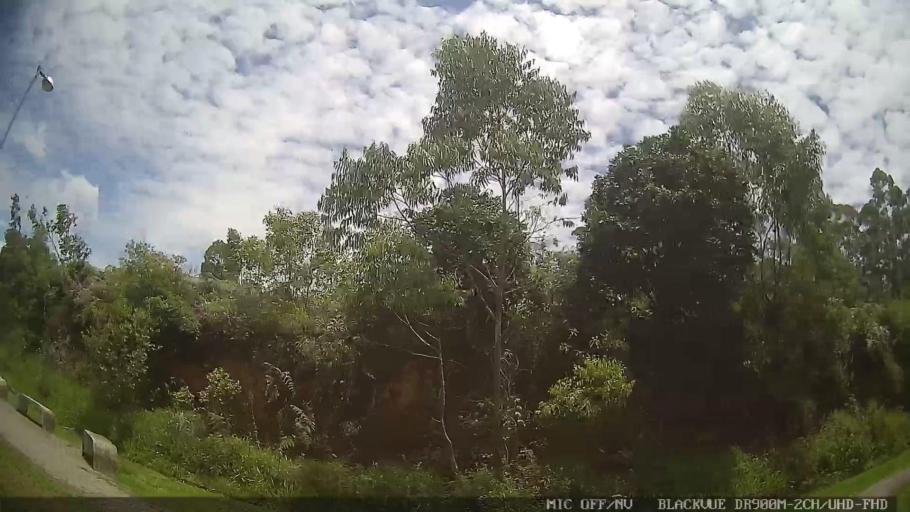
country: BR
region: Sao Paulo
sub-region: Biritiba-Mirim
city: Biritiba Mirim
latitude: -23.5492
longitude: -45.9662
